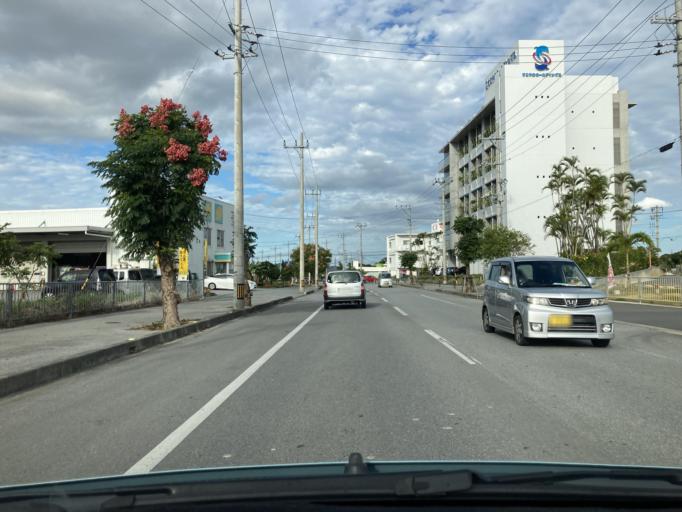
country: JP
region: Okinawa
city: Okinawa
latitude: 26.3690
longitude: 127.8259
